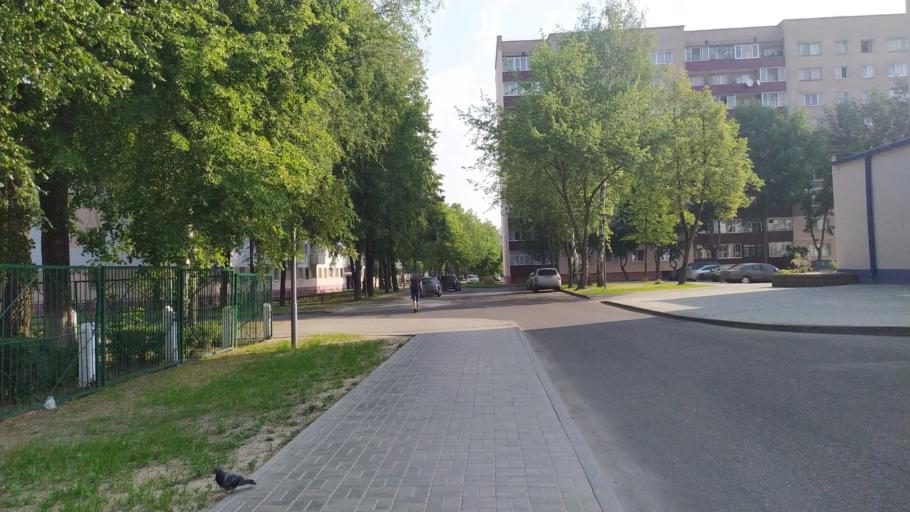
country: BY
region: Vitebsk
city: Navapolatsk
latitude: 55.5320
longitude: 28.6511
